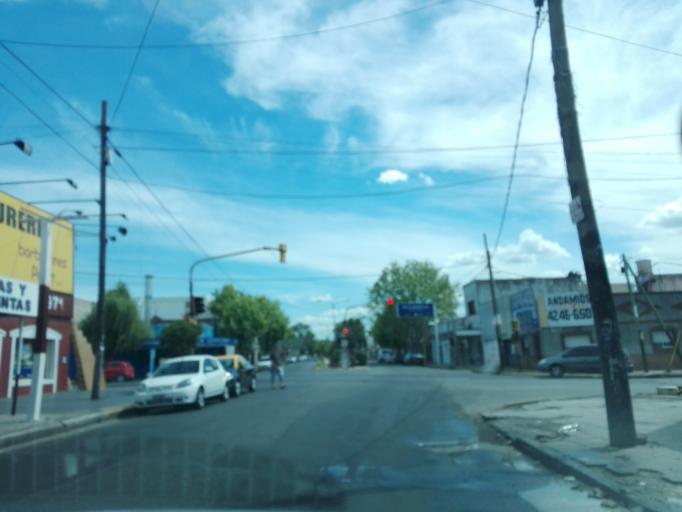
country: AR
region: Buenos Aires
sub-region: Partido de Lanus
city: Lanus
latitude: -34.7109
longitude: -58.3768
